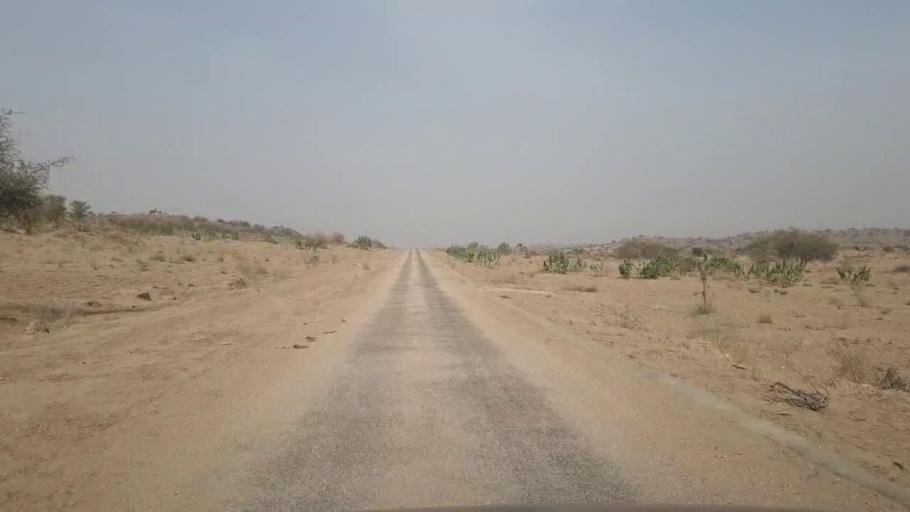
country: PK
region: Sindh
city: Chor
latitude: 25.6212
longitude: 69.9354
